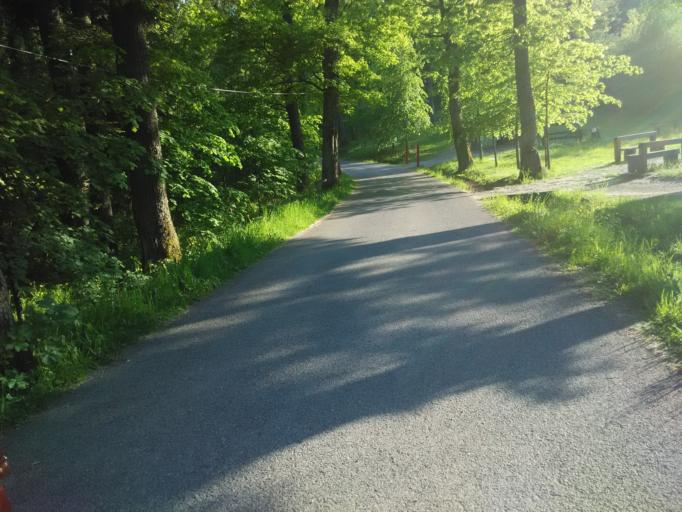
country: SK
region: Presovsky
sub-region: Okres Presov
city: Levoca
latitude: 49.0448
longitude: 20.6002
